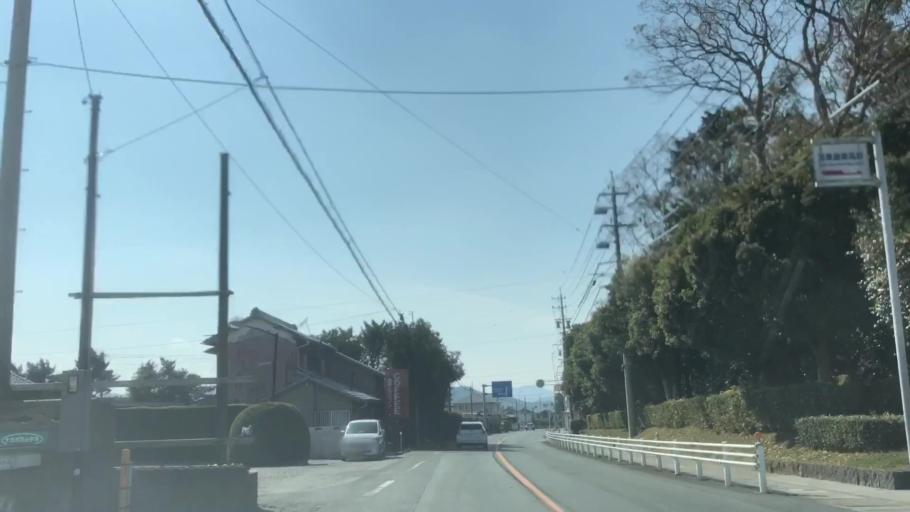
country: JP
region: Aichi
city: Tahara
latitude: 34.6563
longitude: 137.2455
